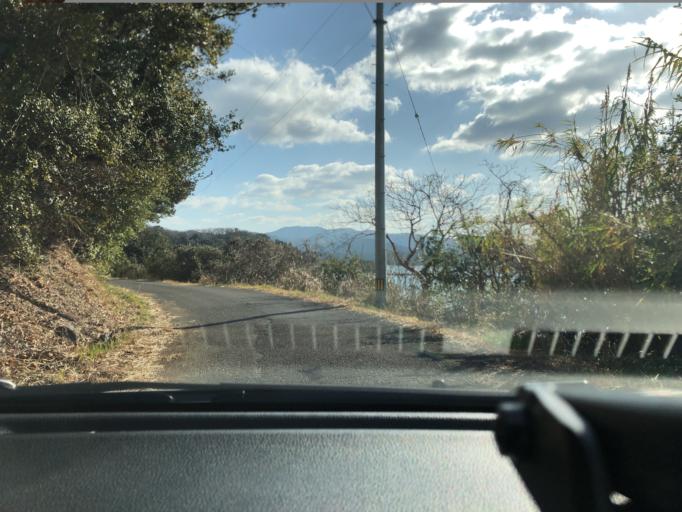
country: JP
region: Kochi
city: Sukumo
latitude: 32.9129
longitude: 132.6895
